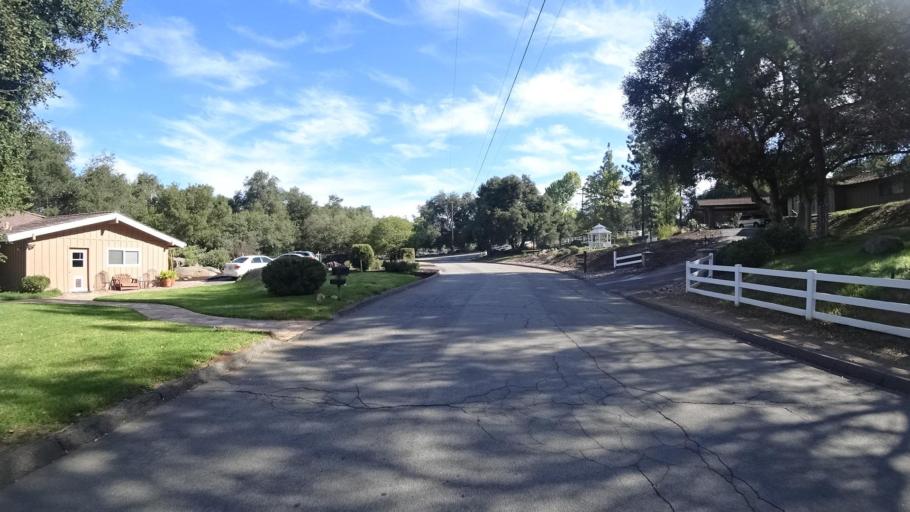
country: US
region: California
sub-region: San Diego County
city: Alpine
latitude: 32.8190
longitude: -116.7520
